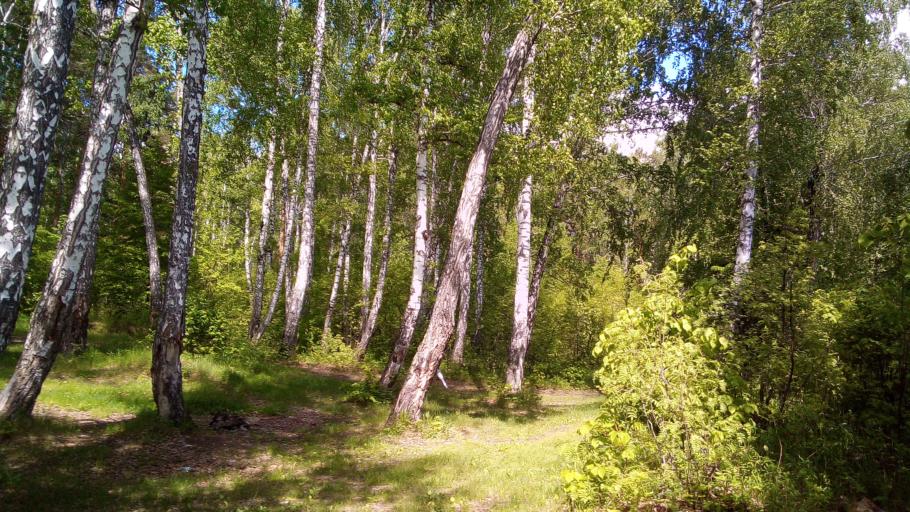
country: RU
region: Chelyabinsk
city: Chebarkul'
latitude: 55.0826
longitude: 60.3822
